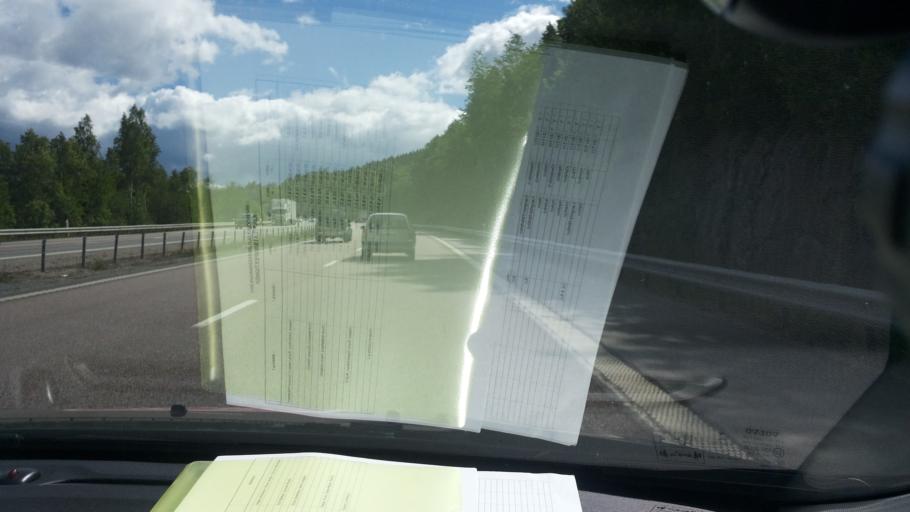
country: SE
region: Vaesternorrland
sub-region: Timra Kommun
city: Timra
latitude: 62.4703
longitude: 17.3149
